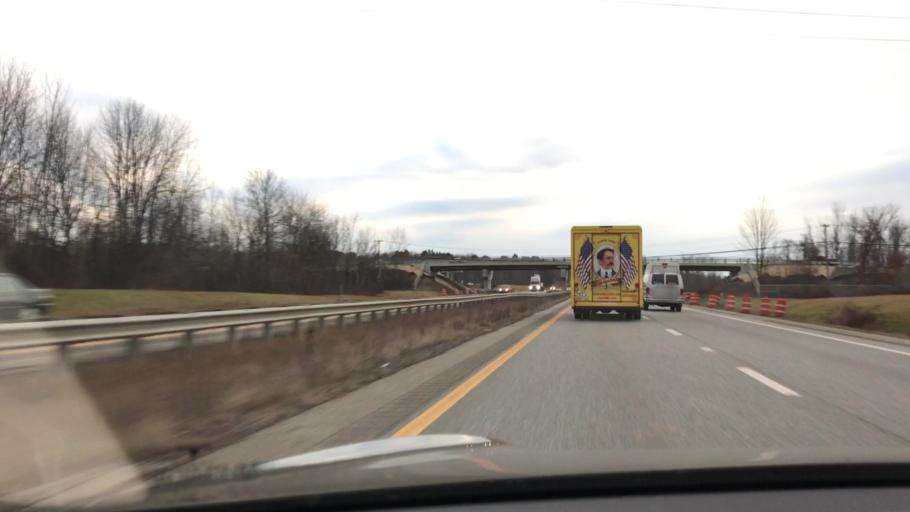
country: US
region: Maine
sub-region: Kennebec County
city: Hallowell
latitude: 44.2988
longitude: -69.8075
